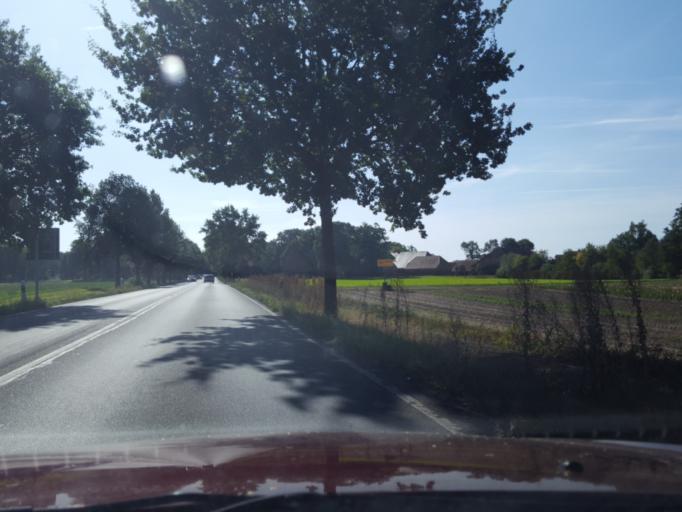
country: DE
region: Lower Saxony
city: Eystrup
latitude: 52.8008
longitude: 9.2086
